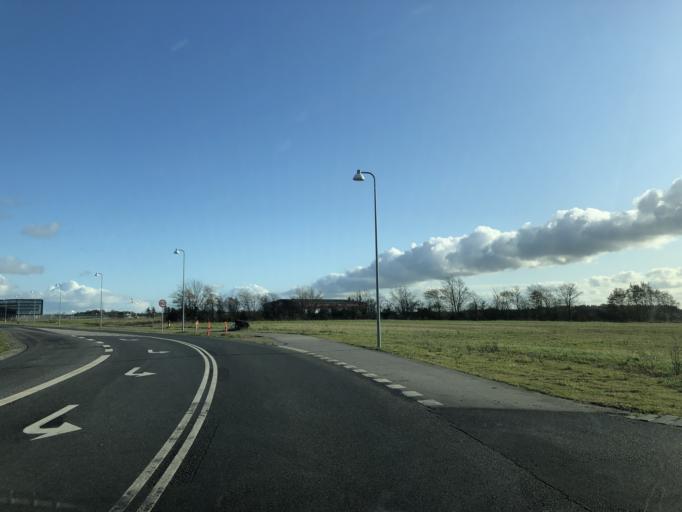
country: DK
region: Central Jutland
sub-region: Ikast-Brande Kommune
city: Bording Kirkeby
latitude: 56.1333
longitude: 9.3436
